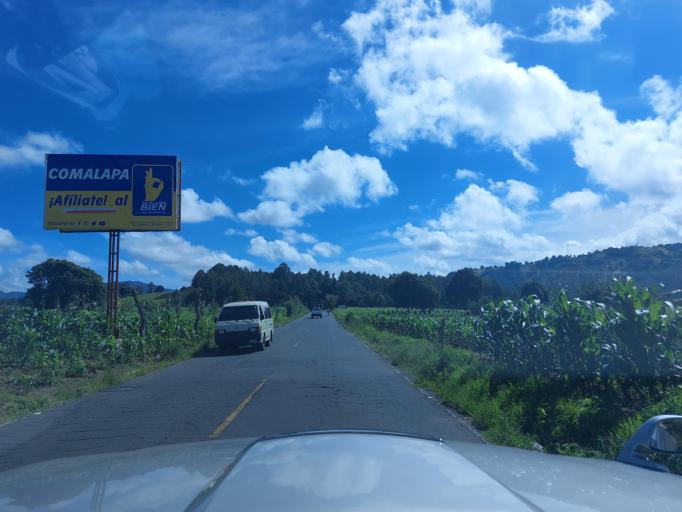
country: GT
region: Chimaltenango
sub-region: Municipio de Santa Cruz Balanya
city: Santa Cruz Balanya
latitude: 14.7032
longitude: -90.8978
